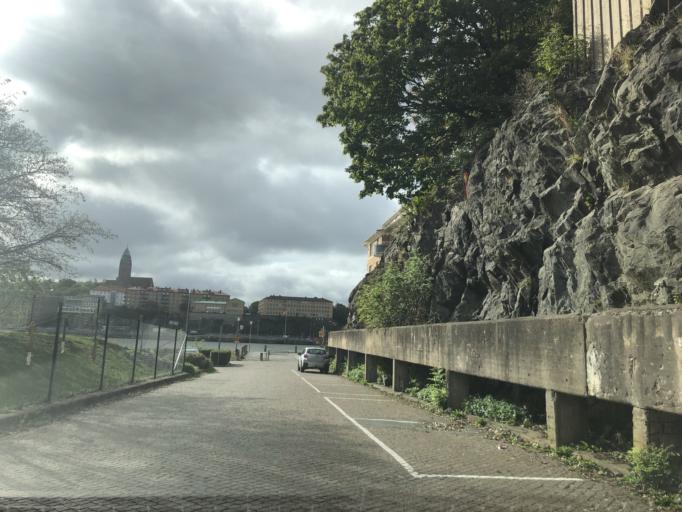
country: SE
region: Vaestra Goetaland
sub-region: Goteborg
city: Majorna
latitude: 57.7036
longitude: 11.9335
